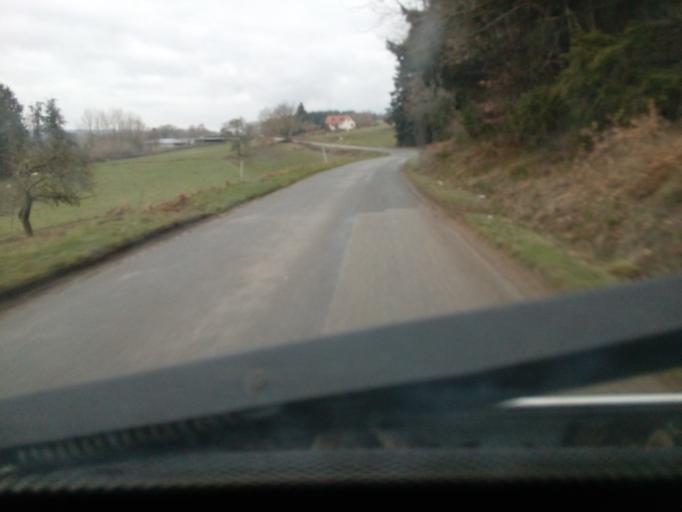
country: FR
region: Limousin
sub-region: Departement de la Creuse
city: Felletin
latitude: 45.8737
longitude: 2.2005
